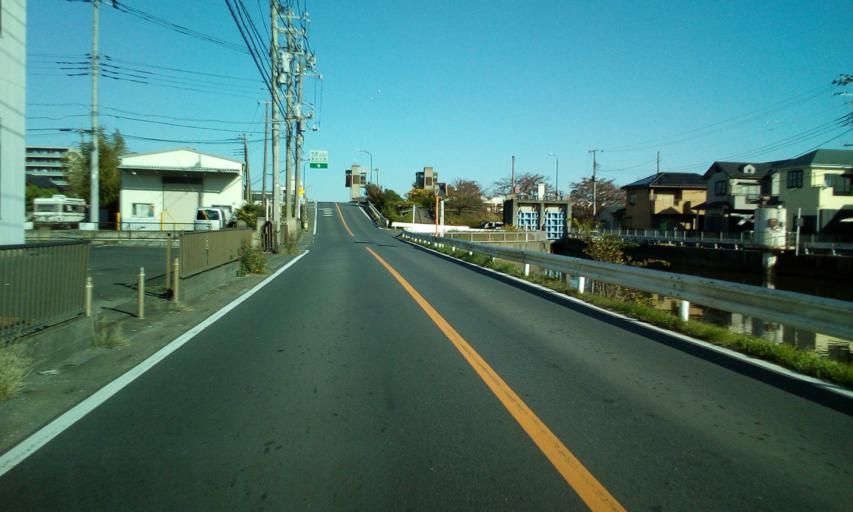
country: JP
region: Chiba
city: Matsudo
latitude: 35.8166
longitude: 139.8836
